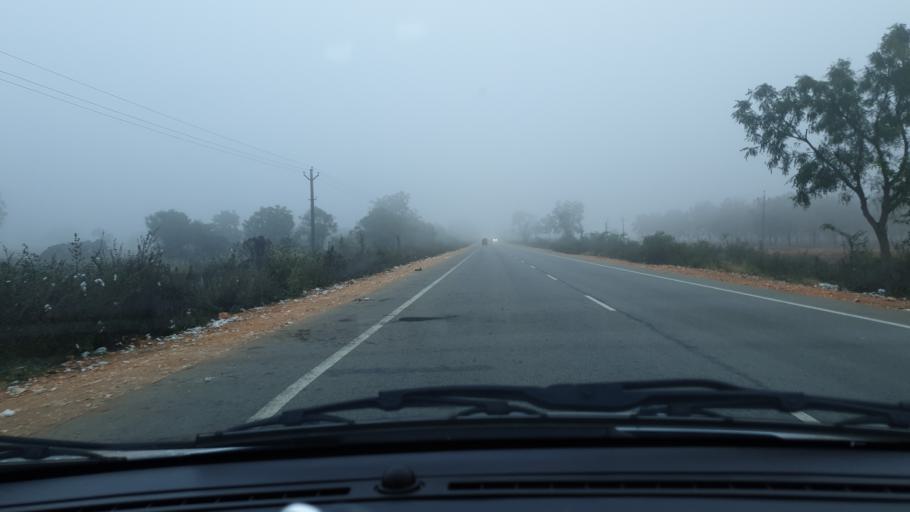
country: IN
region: Telangana
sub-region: Mahbubnagar
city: Nagar Karnul
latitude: 16.6354
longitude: 78.6016
